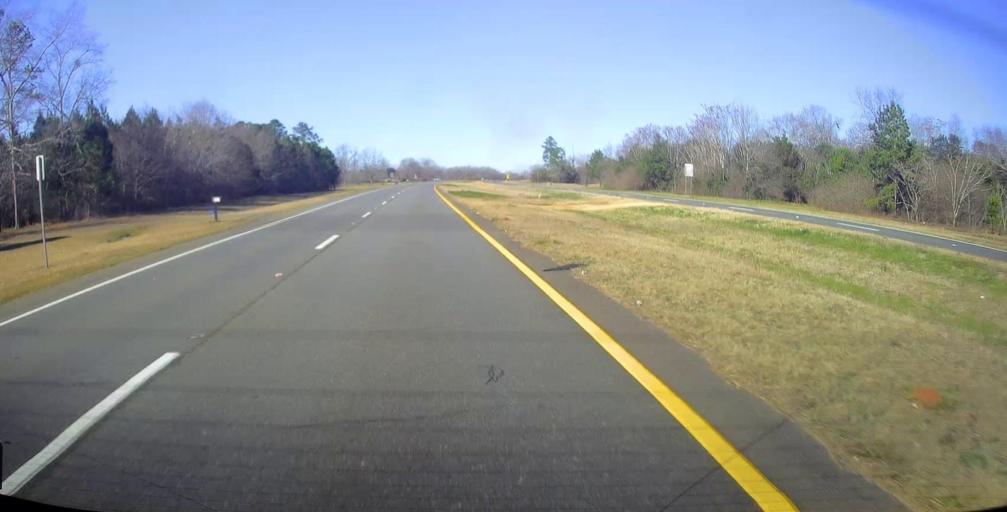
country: US
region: Georgia
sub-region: Sumter County
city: Americus
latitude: 32.1527
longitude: -84.2702
